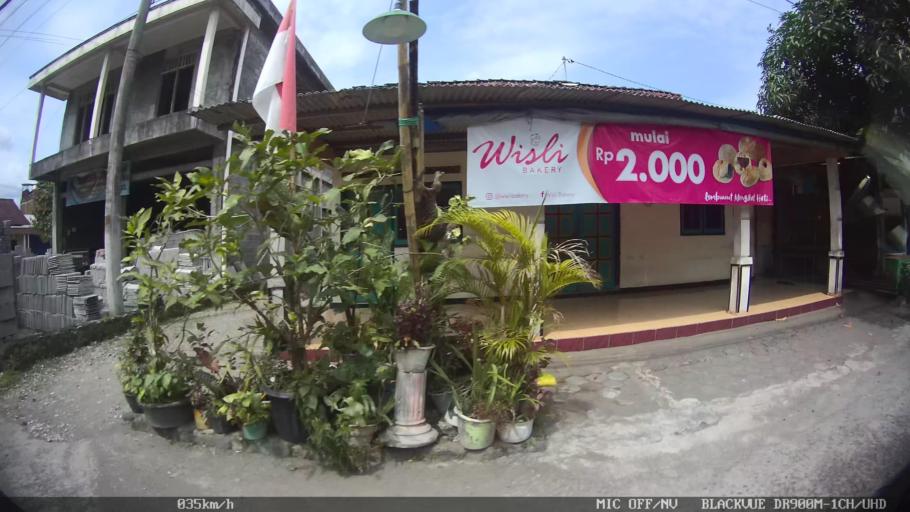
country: ID
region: Daerah Istimewa Yogyakarta
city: Depok
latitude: -7.7494
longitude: 110.4490
